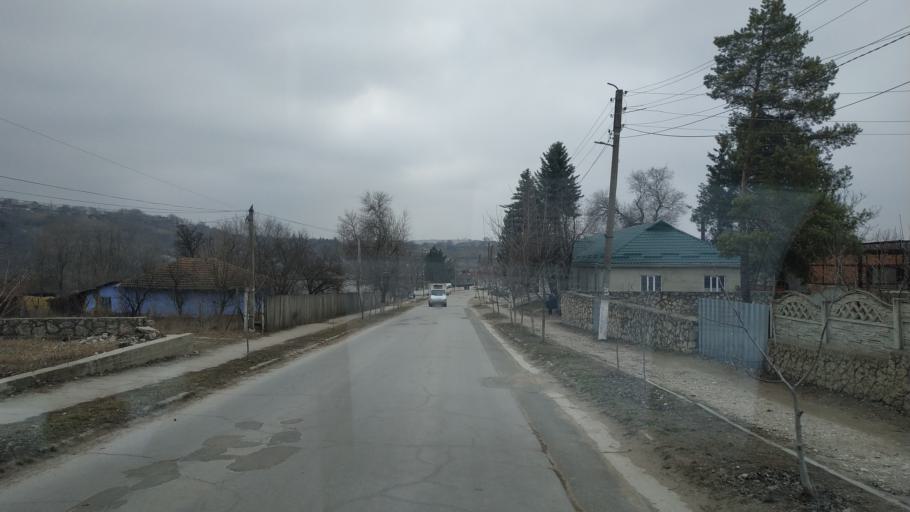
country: MD
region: Hincesti
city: Hincesti
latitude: 46.8835
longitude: 28.4113
